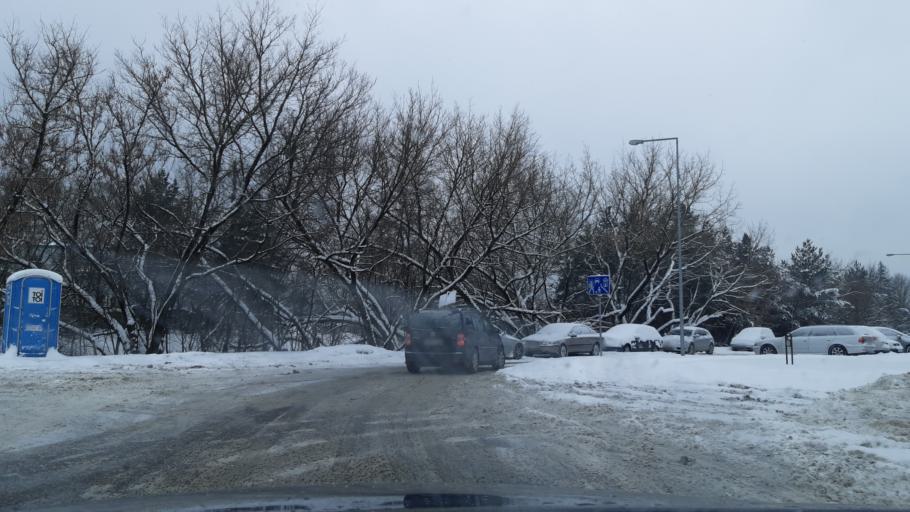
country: LT
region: Vilnius County
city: Vilkpede
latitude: 54.6656
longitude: 25.2450
